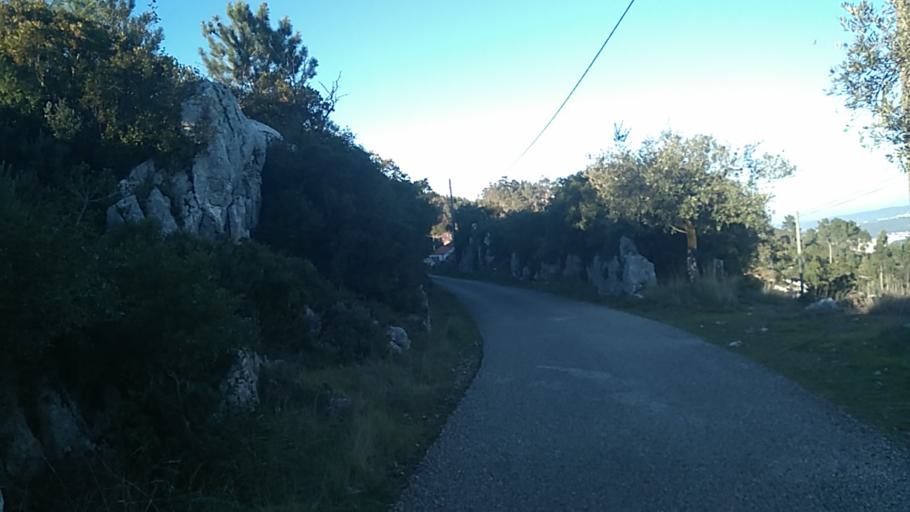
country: PT
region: Leiria
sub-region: Porto de Mos
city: Porto de Mos
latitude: 39.5570
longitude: -8.8431
